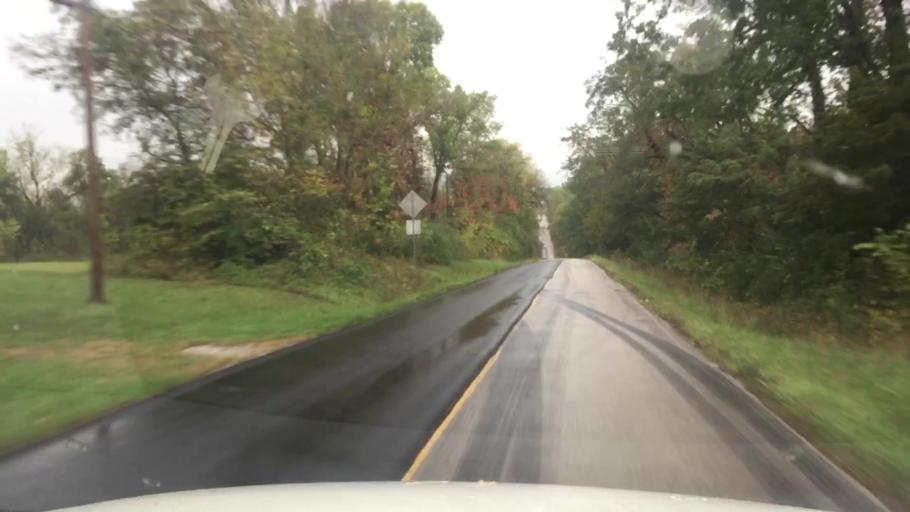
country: US
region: Missouri
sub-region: Boone County
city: Columbia
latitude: 38.9354
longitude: -92.4965
